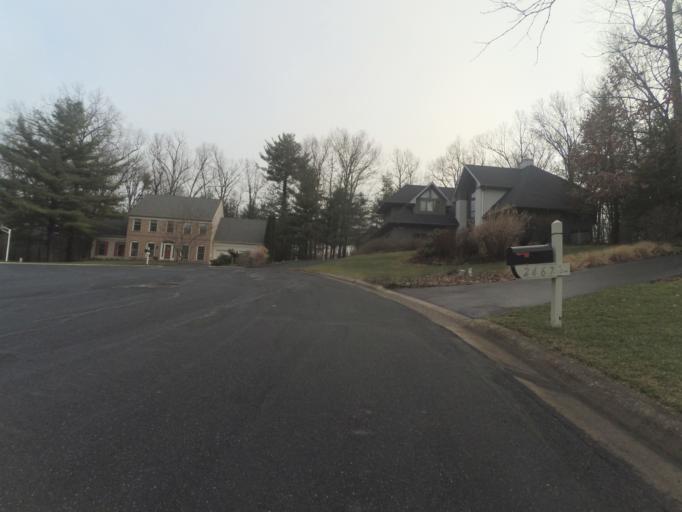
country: US
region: Pennsylvania
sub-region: Centre County
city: Park Forest Village
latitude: 40.7884
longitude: -77.9169
